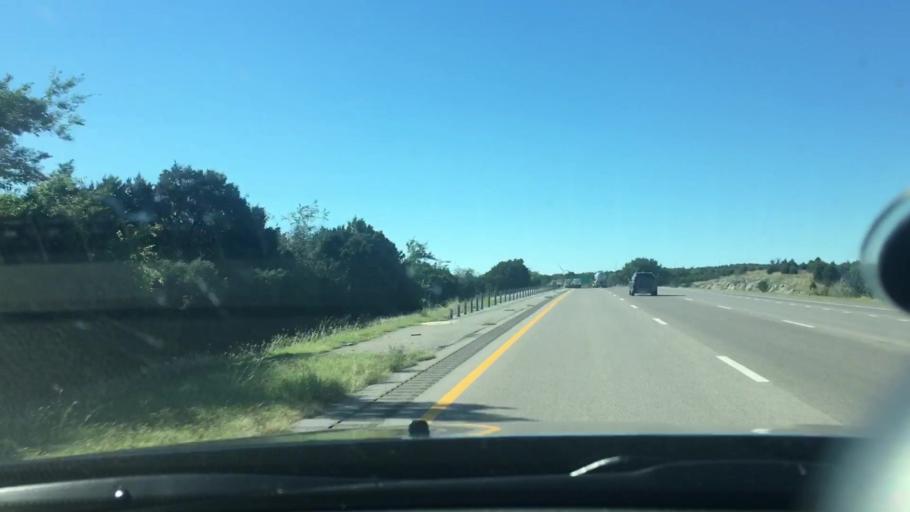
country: US
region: Oklahoma
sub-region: Murray County
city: Davis
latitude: 34.4213
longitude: -97.1358
